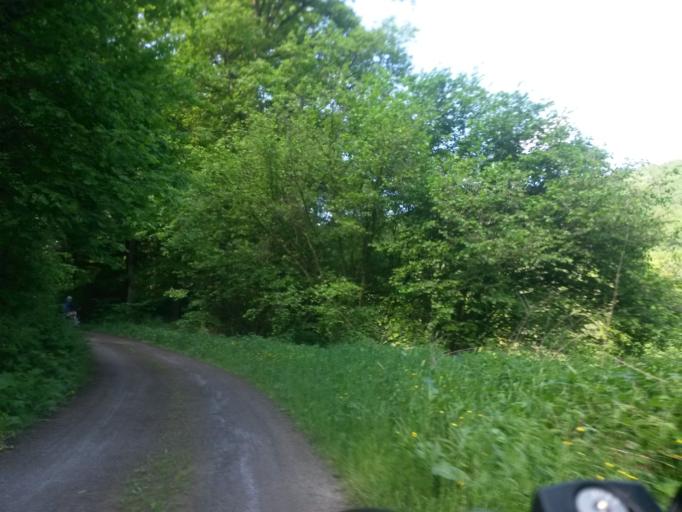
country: DE
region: Bavaria
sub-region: Regierungsbezirk Unterfranken
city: Euerdorf
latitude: 50.1700
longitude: 10.0502
